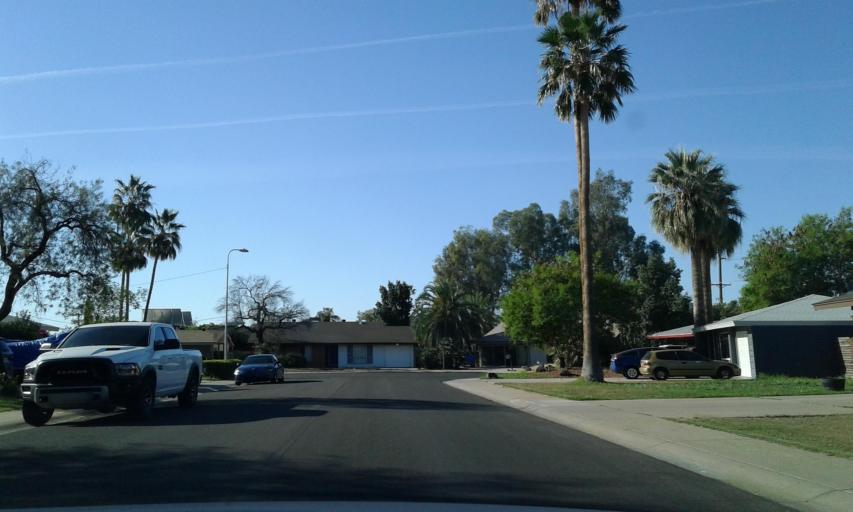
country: US
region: Arizona
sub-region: Maricopa County
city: Glendale
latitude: 33.5405
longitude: -112.1078
